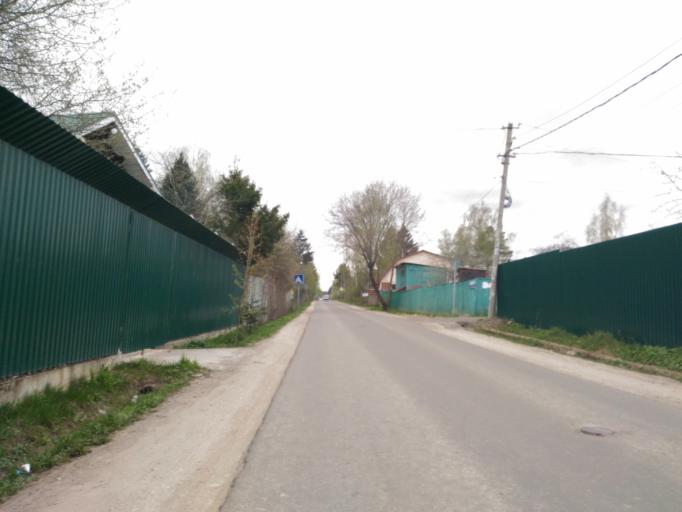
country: RU
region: Moskovskaya
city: Dedovsk
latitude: 55.8506
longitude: 37.1460
